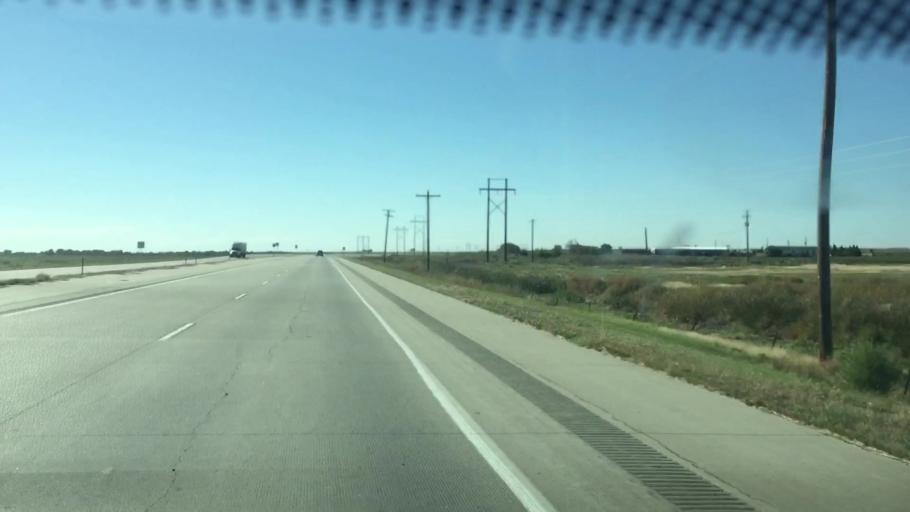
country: US
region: Colorado
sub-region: Prowers County
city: Lamar
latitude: 38.1090
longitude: -102.6919
